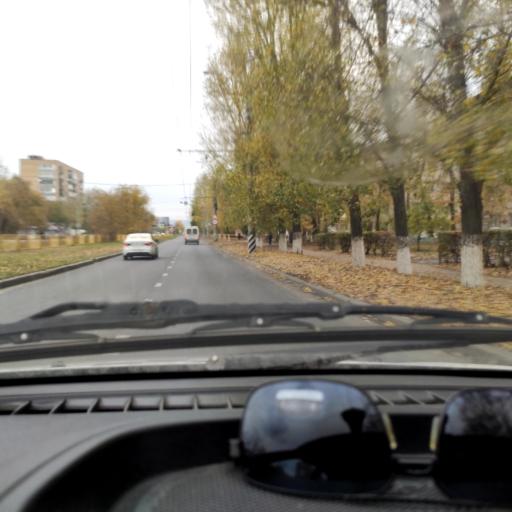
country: RU
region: Samara
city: Zhigulevsk
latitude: 53.4853
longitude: 49.4740
